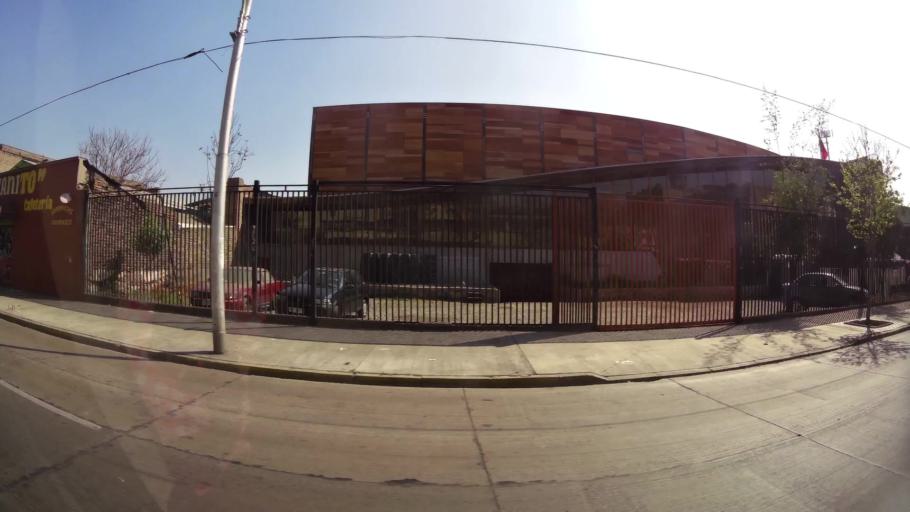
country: CL
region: Santiago Metropolitan
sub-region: Provincia de Santiago
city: Santiago
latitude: -33.4455
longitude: -70.6795
